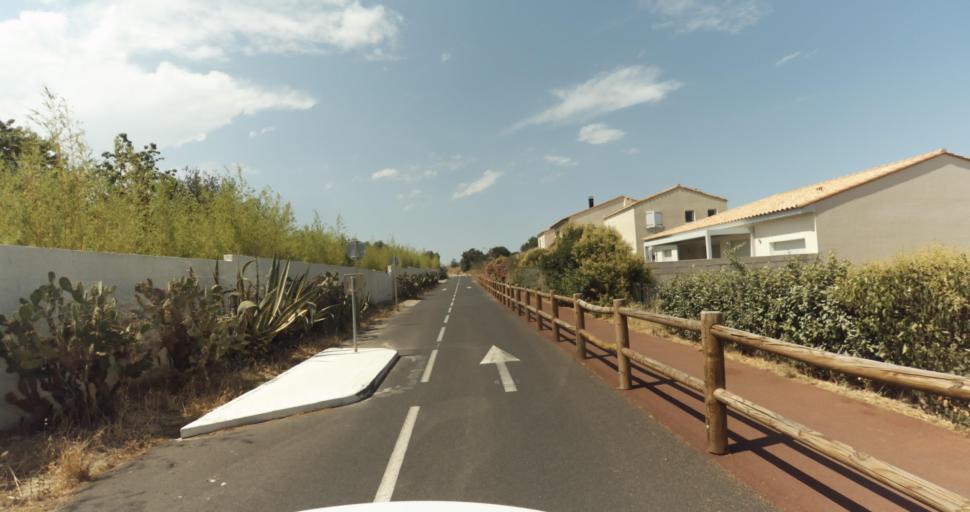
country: FR
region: Languedoc-Roussillon
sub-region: Departement des Pyrenees-Orientales
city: Latour-Bas-Elne
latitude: 42.6094
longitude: 2.9917
